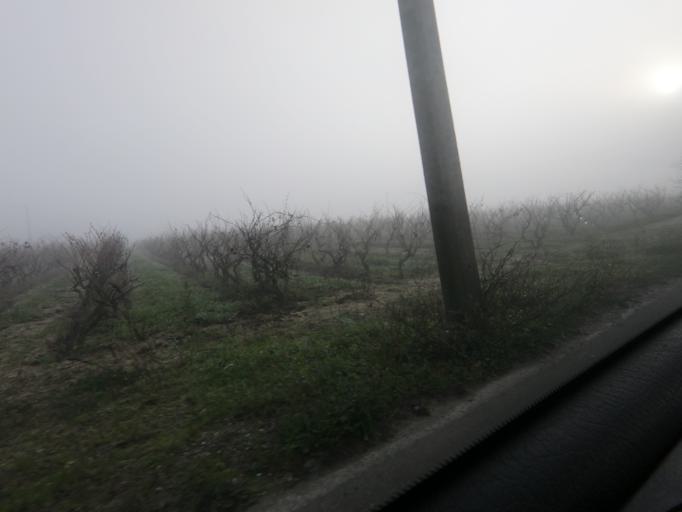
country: PT
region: Setubal
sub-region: Palmela
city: Palmela
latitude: 38.6040
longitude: -8.8496
